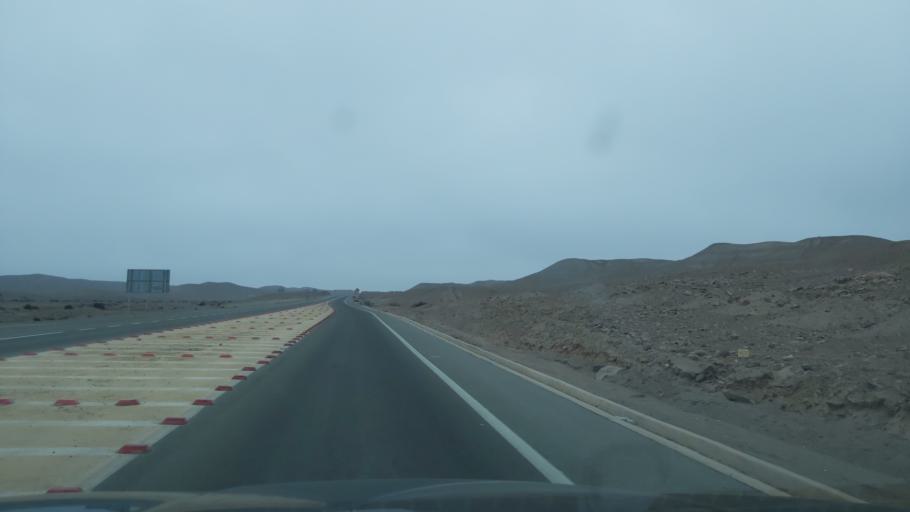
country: CL
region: Atacama
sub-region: Provincia de Copiapo
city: Copiapo
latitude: -27.2896
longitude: -70.1446
